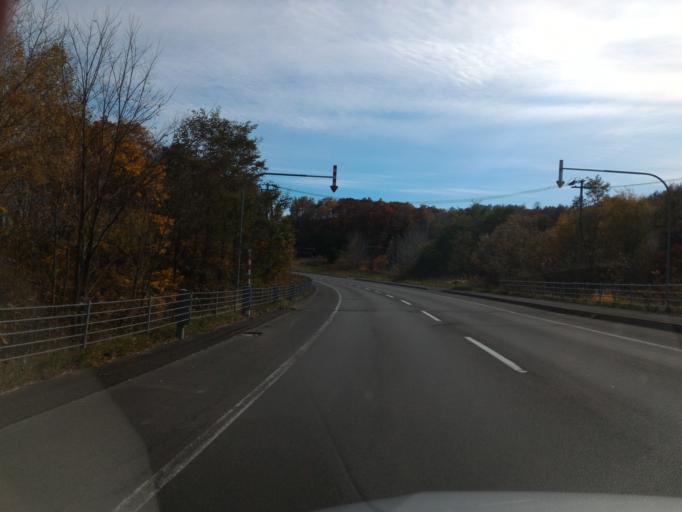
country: JP
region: Hokkaido
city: Shimo-furano
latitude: 43.3691
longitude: 142.3483
